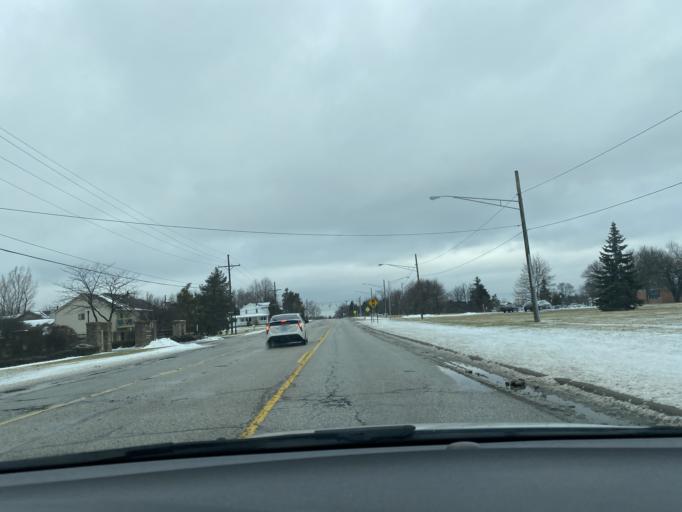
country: US
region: Michigan
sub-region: Lapeer County
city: Lapeer
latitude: 43.0552
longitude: -83.3427
